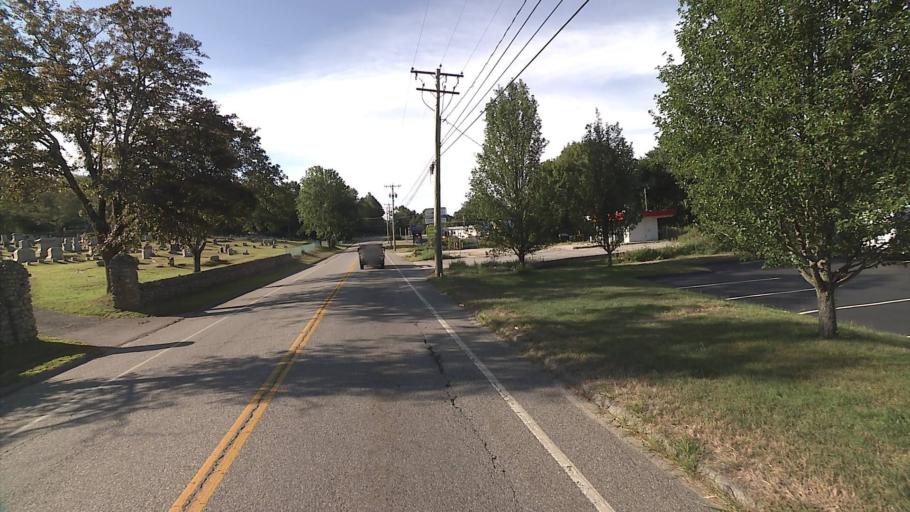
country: US
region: Connecticut
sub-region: New London County
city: Uncasville
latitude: 41.4243
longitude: -72.1101
